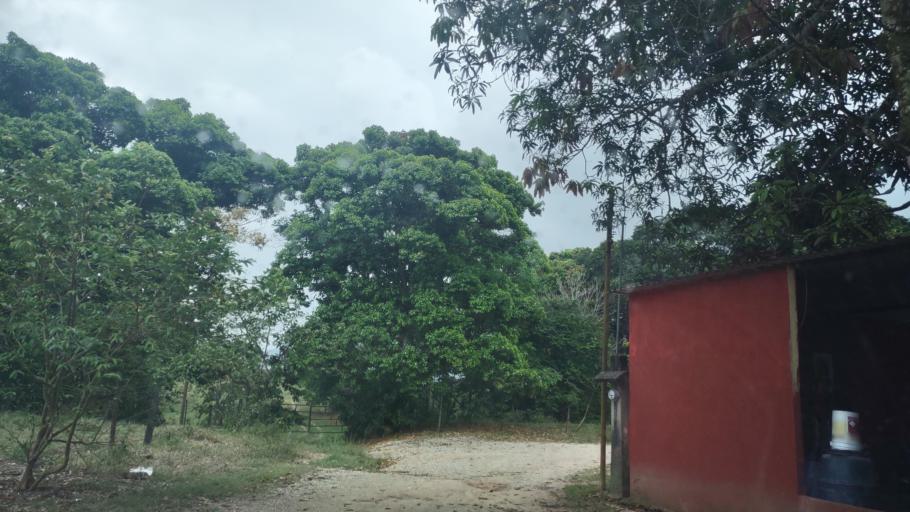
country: MX
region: Veracruz
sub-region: Uxpanapa
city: Poblado 10
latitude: 17.4980
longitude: -94.1594
